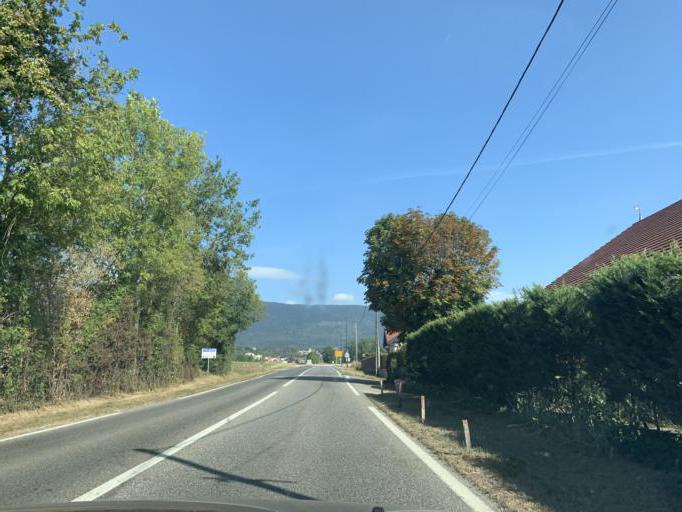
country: FR
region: Rhone-Alpes
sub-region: Departement de l'Ain
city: Echenevex
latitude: 46.3149
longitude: 6.0508
